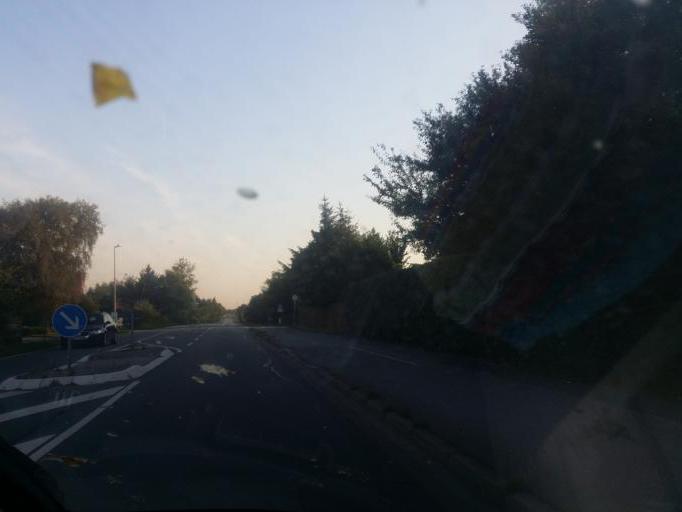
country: DE
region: Schleswig-Holstein
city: Husum
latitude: 54.4894
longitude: 9.0455
